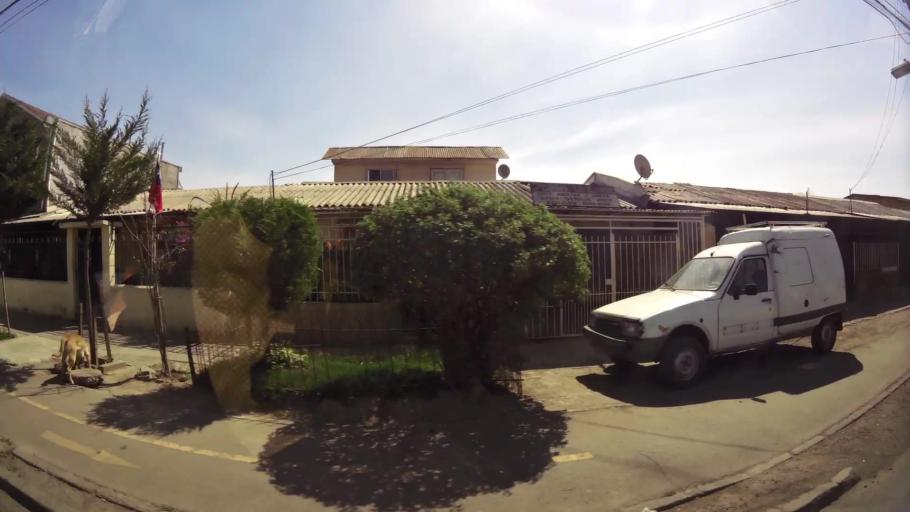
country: CL
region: Santiago Metropolitan
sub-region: Provincia de Maipo
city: San Bernardo
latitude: -33.5288
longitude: -70.7011
